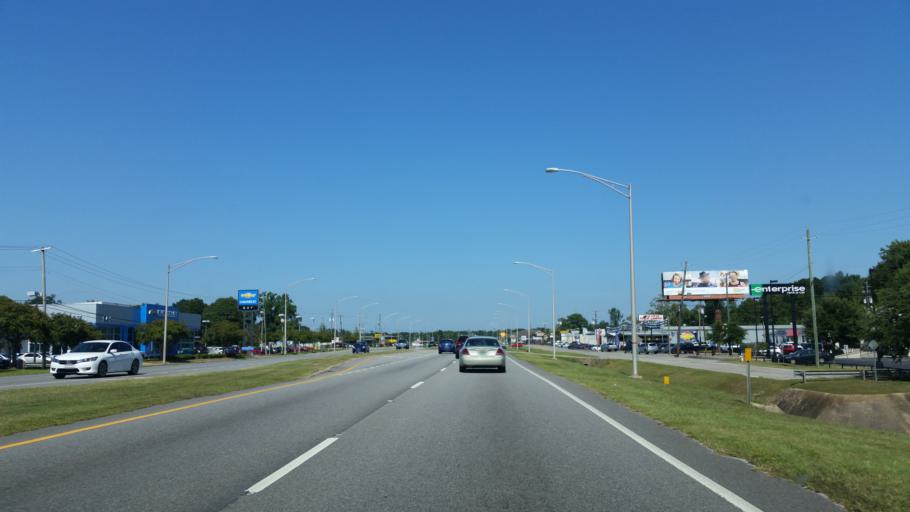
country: US
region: Alabama
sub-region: Mobile County
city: Mobile
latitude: 30.6572
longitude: -88.1137
